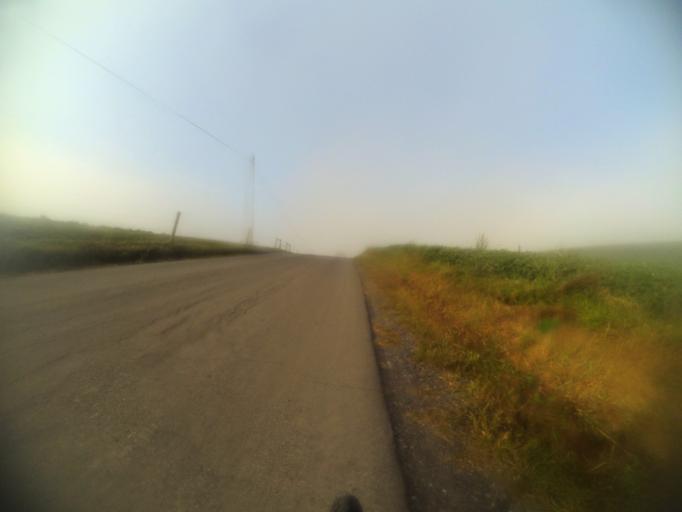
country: US
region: Pennsylvania
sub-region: Centre County
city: Centre Hall
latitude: 40.8712
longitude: -77.6276
